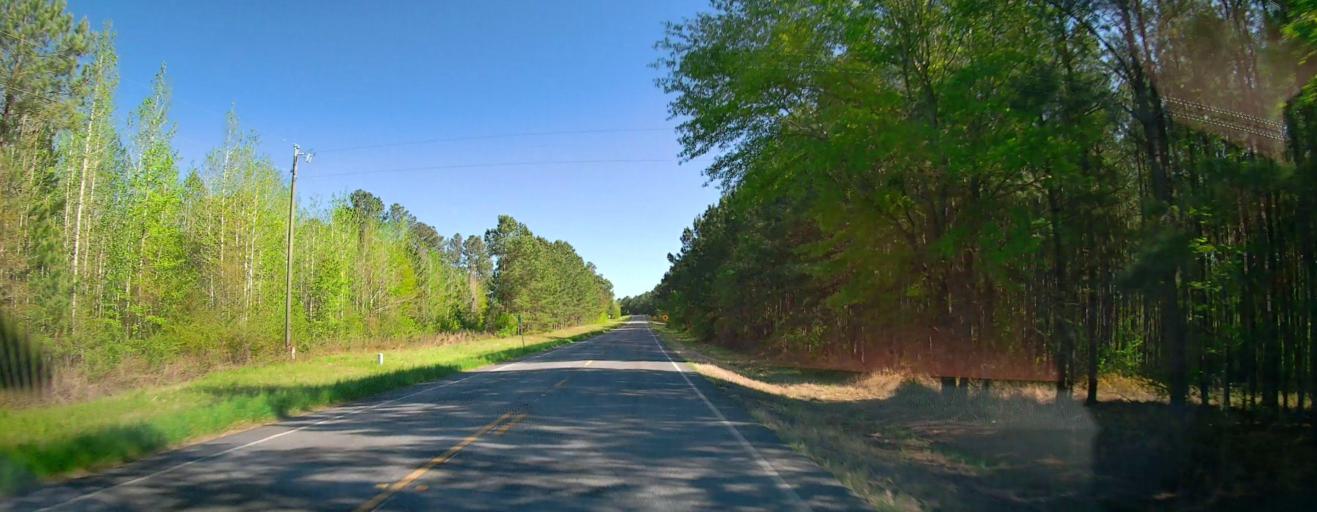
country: US
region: Georgia
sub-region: Wilcox County
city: Rochelle
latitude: 32.0167
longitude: -83.4959
